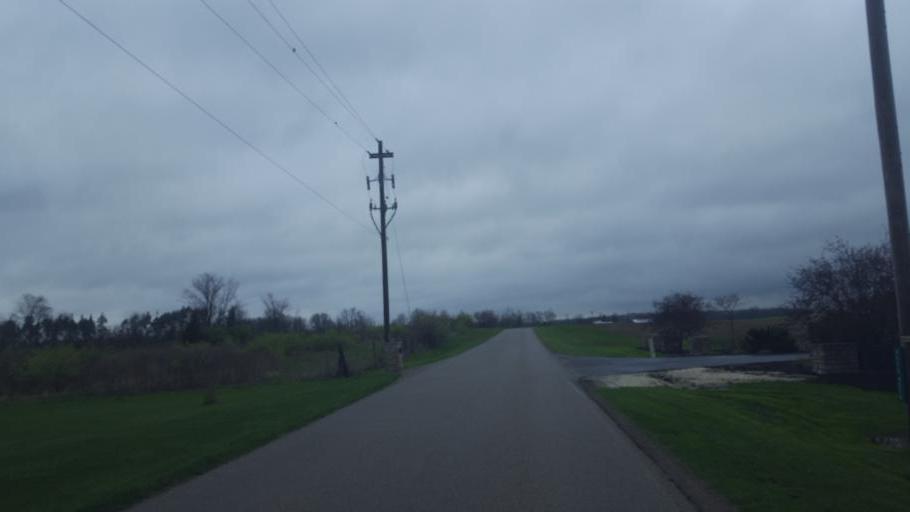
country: US
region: Ohio
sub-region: Morrow County
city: Cardington
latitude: 40.5225
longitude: -82.8594
